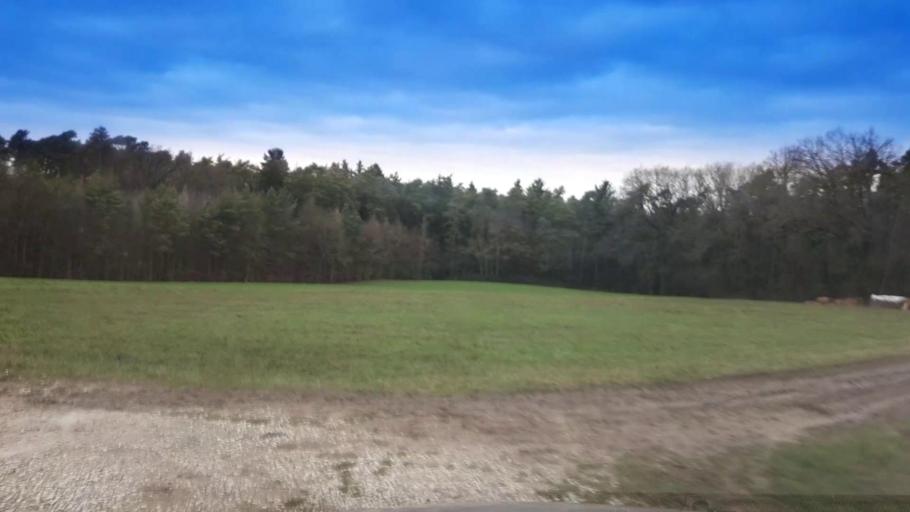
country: DE
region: Bavaria
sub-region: Upper Franconia
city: Burgebrach
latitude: 49.8047
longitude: 10.7855
